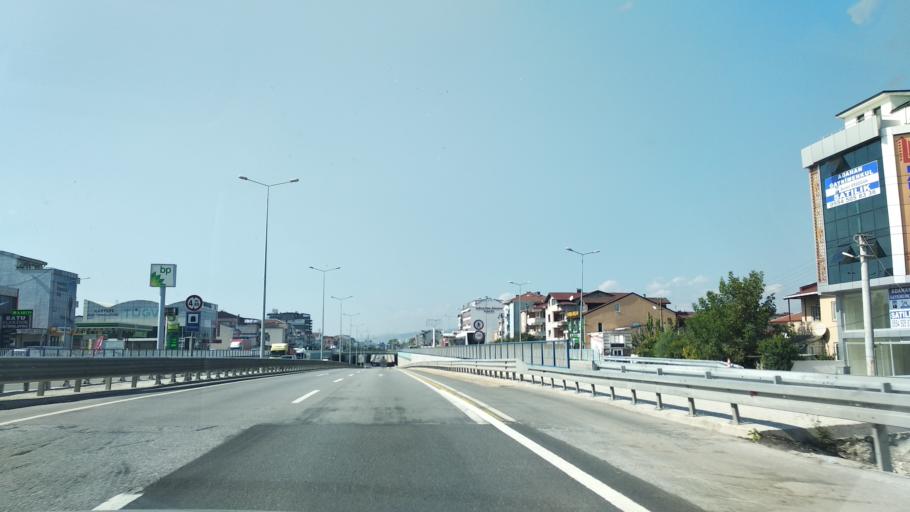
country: TR
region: Kocaeli
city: Kosekoy
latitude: 40.7529
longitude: 30.0275
